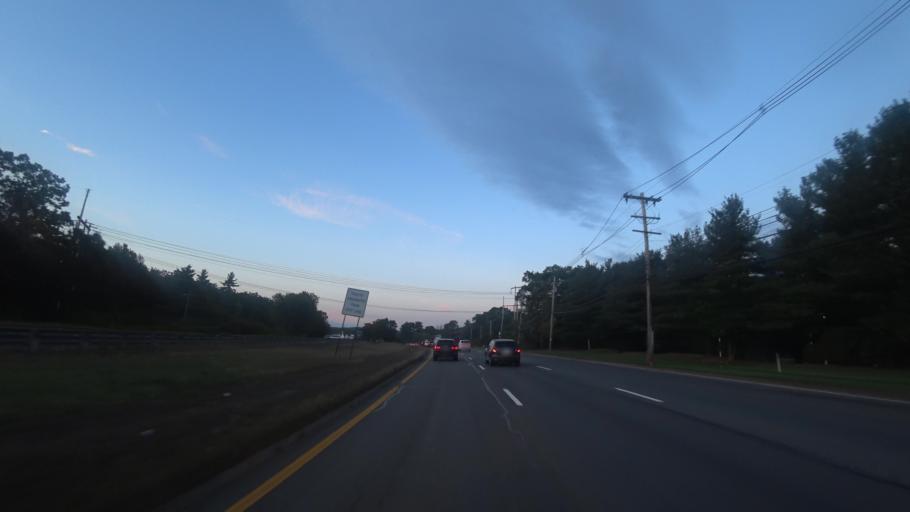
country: US
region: Massachusetts
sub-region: Essex County
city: Saugus
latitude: 42.5091
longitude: -71.0115
